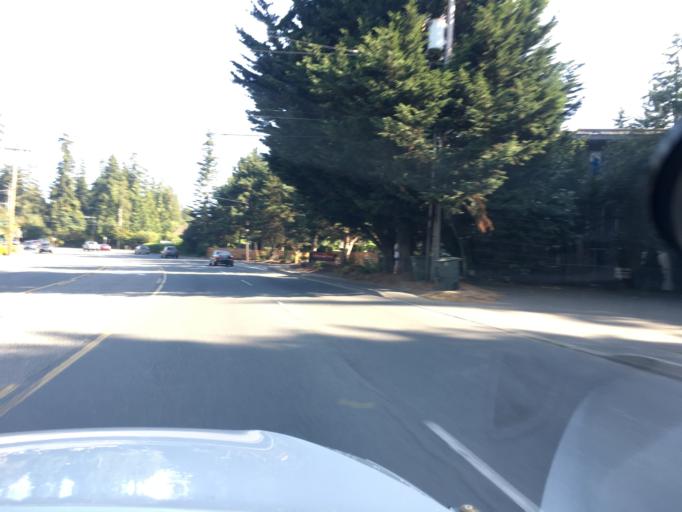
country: US
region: Washington
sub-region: Snohomish County
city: Esperance
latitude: 47.7844
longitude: -122.3531
